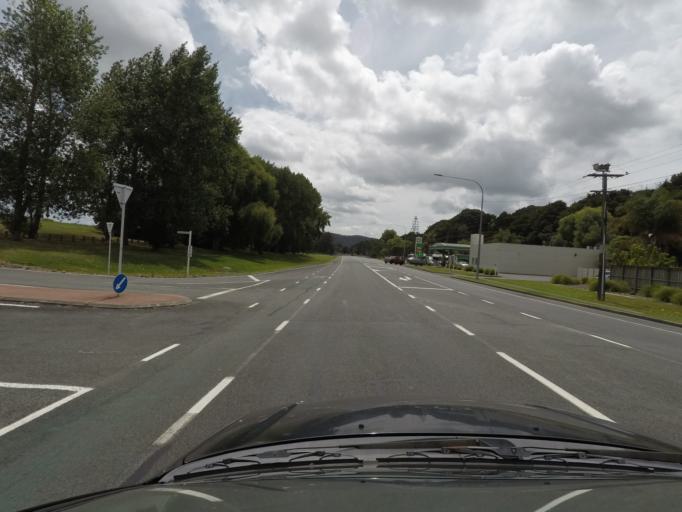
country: NZ
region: Northland
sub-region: Whangarei
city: Whangarei
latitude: -35.7297
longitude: 174.3394
